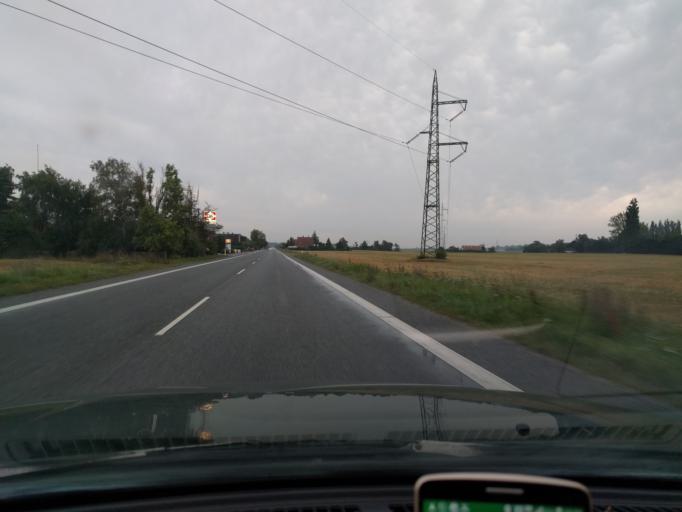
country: DK
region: Zealand
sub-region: Guldborgsund Kommune
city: Norre Alslev
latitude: 54.9441
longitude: 11.8625
